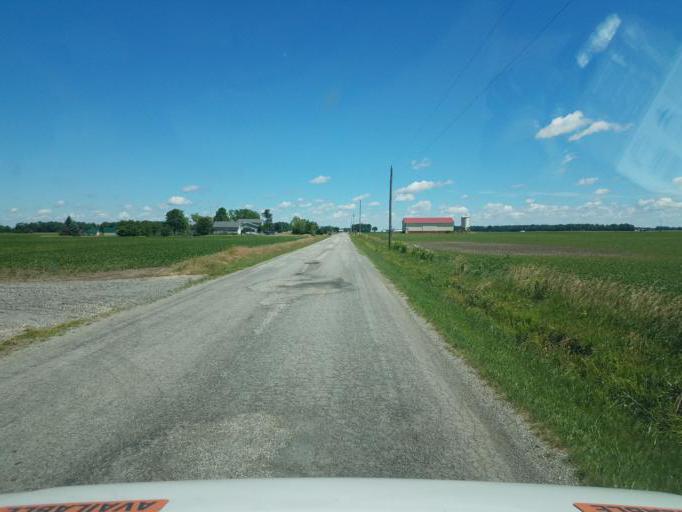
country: US
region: Ohio
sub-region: Morrow County
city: Cardington
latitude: 40.5839
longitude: -82.9385
